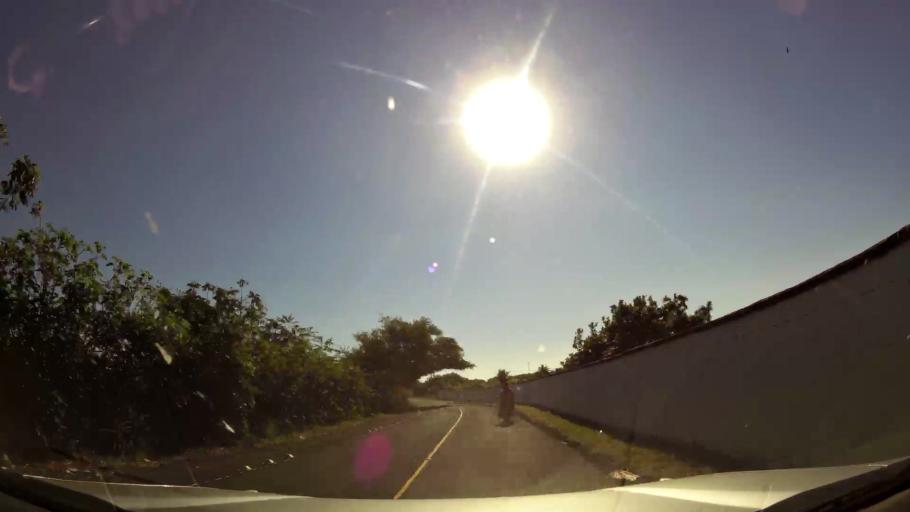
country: GT
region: Santa Rosa
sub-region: Municipio de Taxisco
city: Taxisco
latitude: 13.8889
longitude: -90.4731
